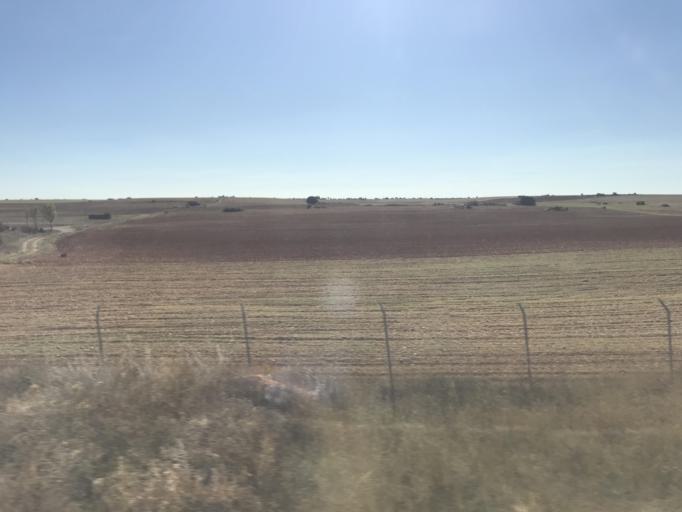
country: ES
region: Castille-La Mancha
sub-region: Provincia de Guadalajara
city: Almadrones
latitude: 40.8655
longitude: -2.7866
